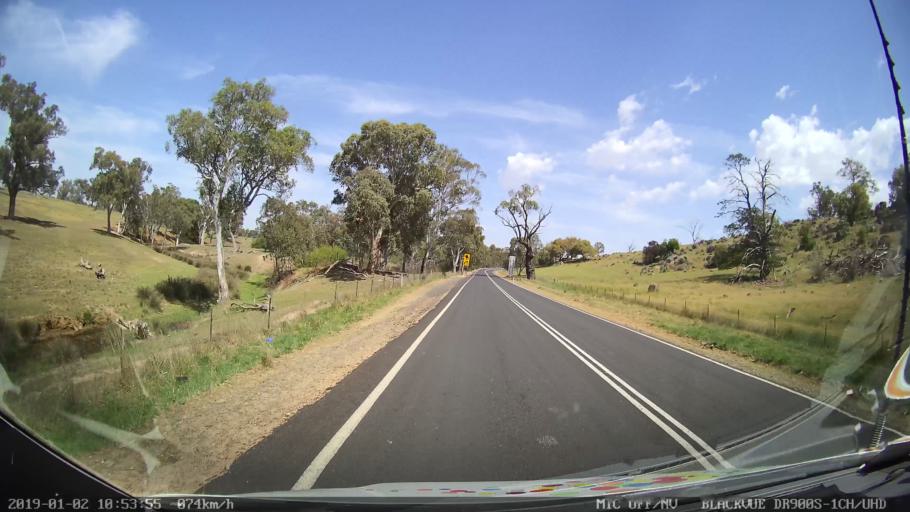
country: AU
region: New South Wales
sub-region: Cootamundra
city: Cootamundra
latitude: -34.6739
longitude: 148.2767
